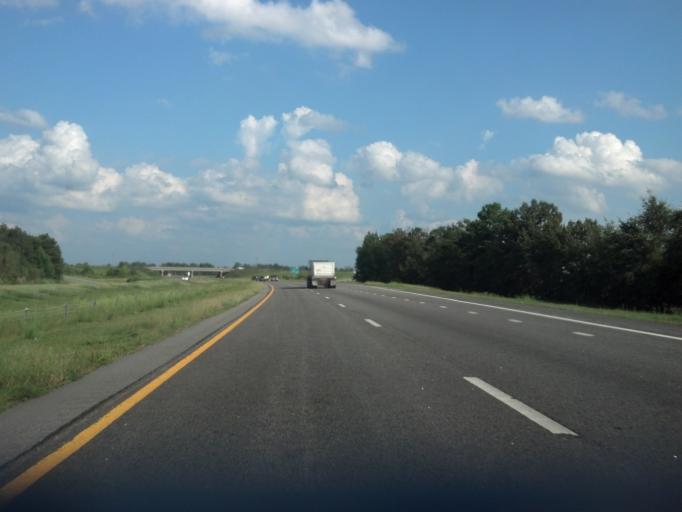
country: US
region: North Carolina
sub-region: Edgecombe County
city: Princeville
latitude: 35.8559
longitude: -77.4674
